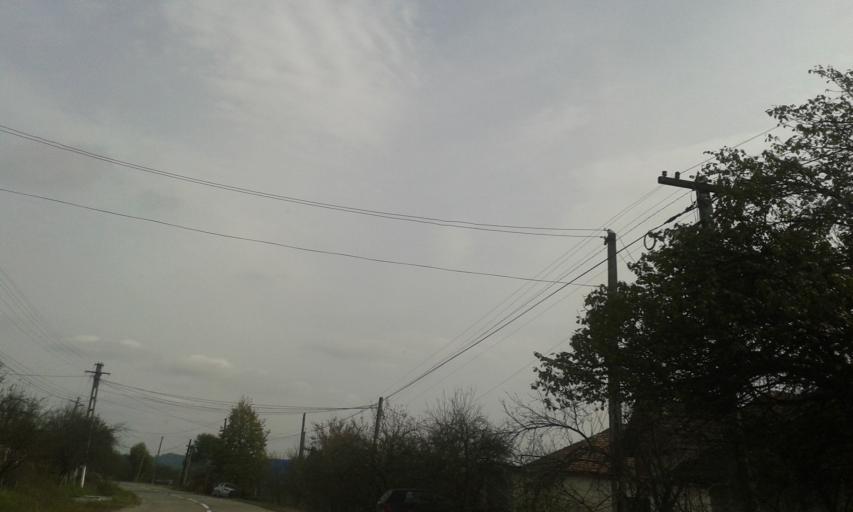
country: RO
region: Valcea
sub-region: Comuna Gradistea
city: Gradistea
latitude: 44.9007
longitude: 23.8085
